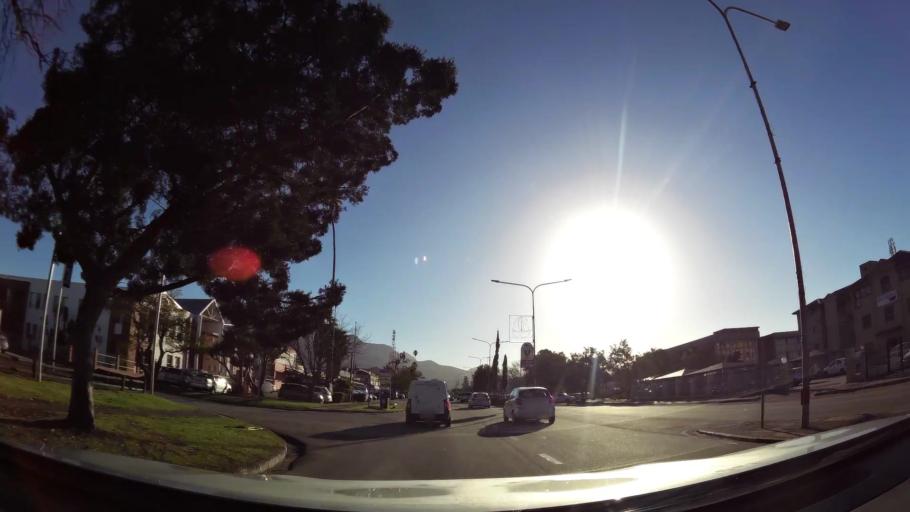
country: ZA
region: Western Cape
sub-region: Eden District Municipality
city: George
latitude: -33.9649
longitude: 22.4518
